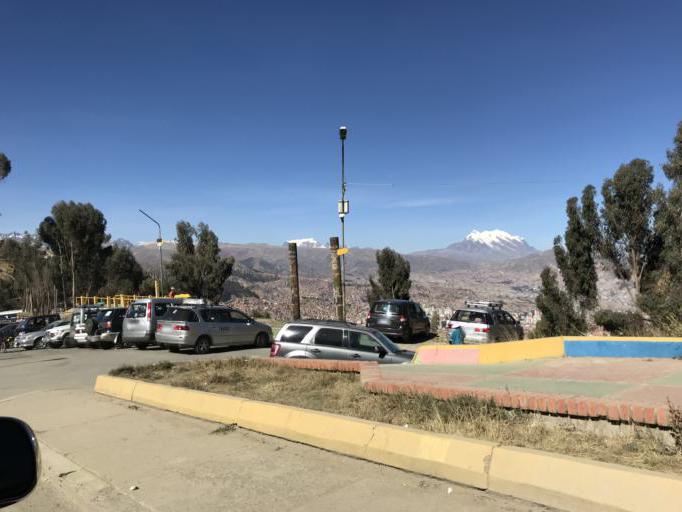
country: BO
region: La Paz
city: La Paz
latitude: -16.4862
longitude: -68.1694
